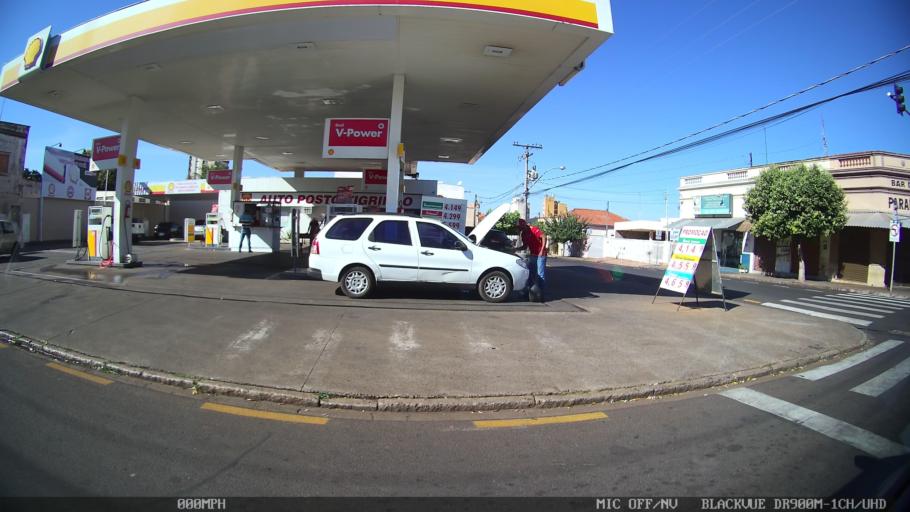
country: BR
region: Sao Paulo
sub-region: Olimpia
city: Olimpia
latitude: -20.7391
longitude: -48.9172
